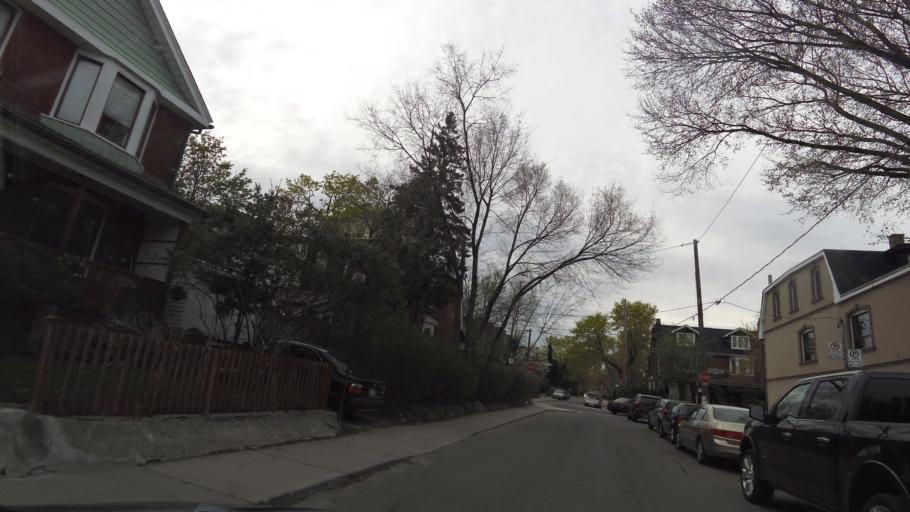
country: CA
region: Ontario
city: Toronto
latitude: 43.6664
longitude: -79.4182
